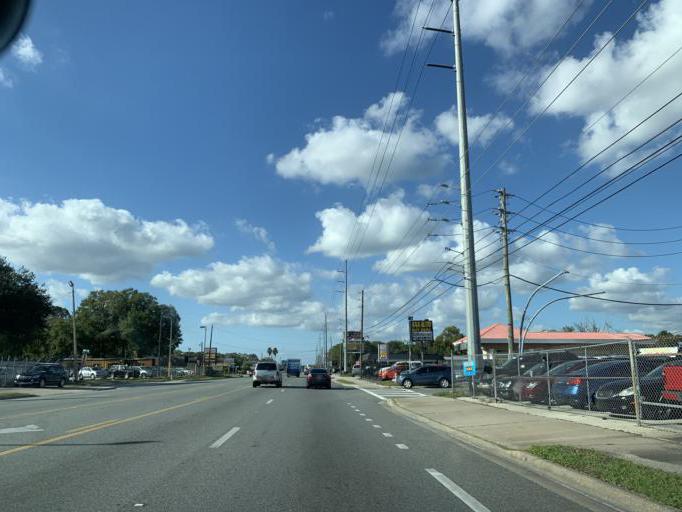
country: US
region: Florida
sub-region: Orange County
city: Fairview Shores
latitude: 28.6061
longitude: -81.4099
